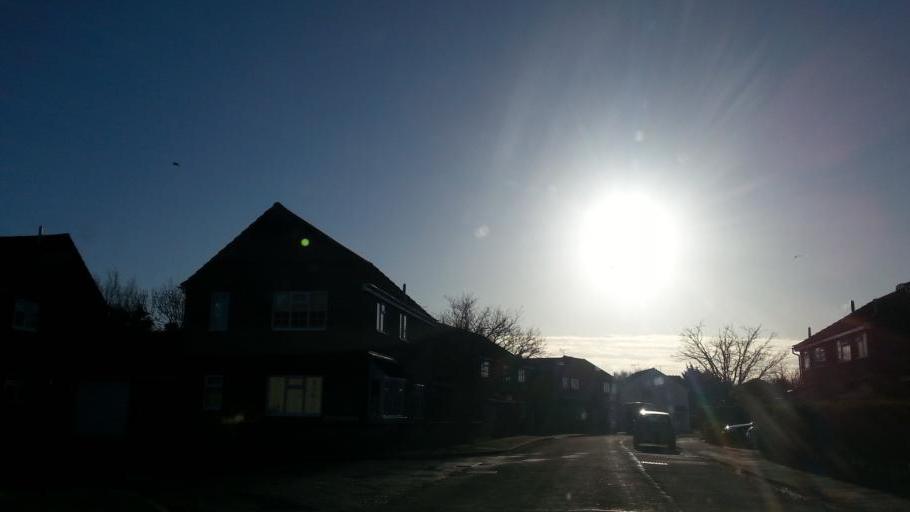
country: GB
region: England
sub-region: Suffolk
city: Felixstowe
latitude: 51.9917
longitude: 1.3148
